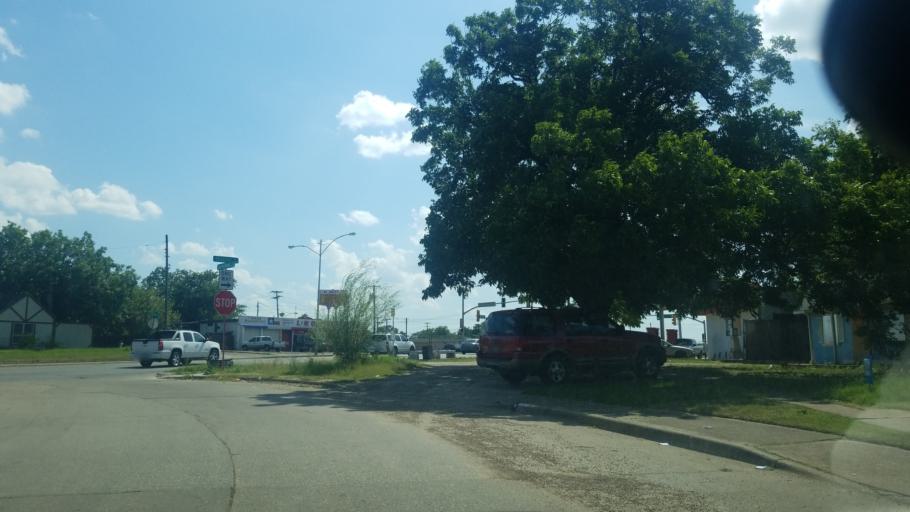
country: US
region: Texas
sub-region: Dallas County
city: Dallas
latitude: 32.7205
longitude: -96.8027
